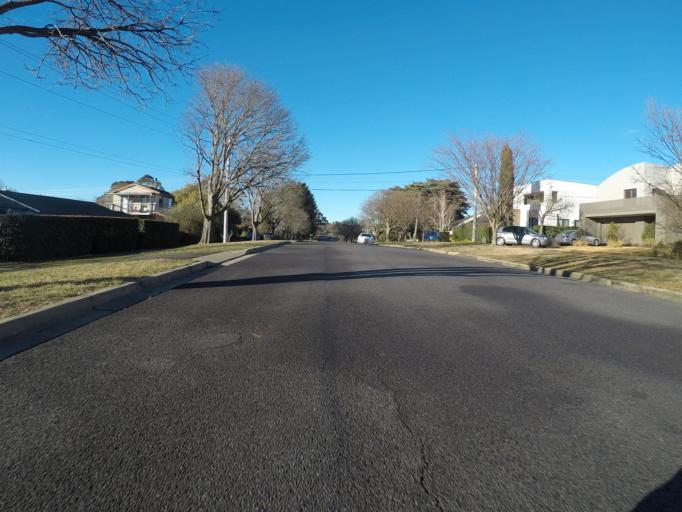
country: AU
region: Australian Capital Territory
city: Forrest
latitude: -35.3047
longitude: 149.0996
